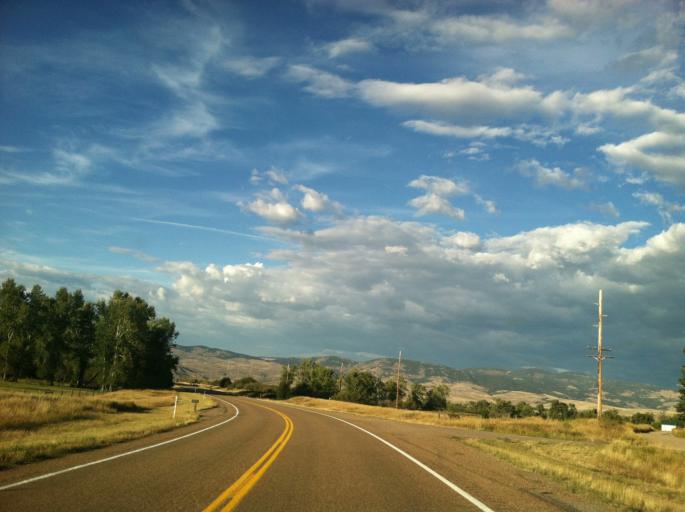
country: US
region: Montana
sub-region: Granite County
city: Philipsburg
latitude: 46.6113
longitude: -113.1792
